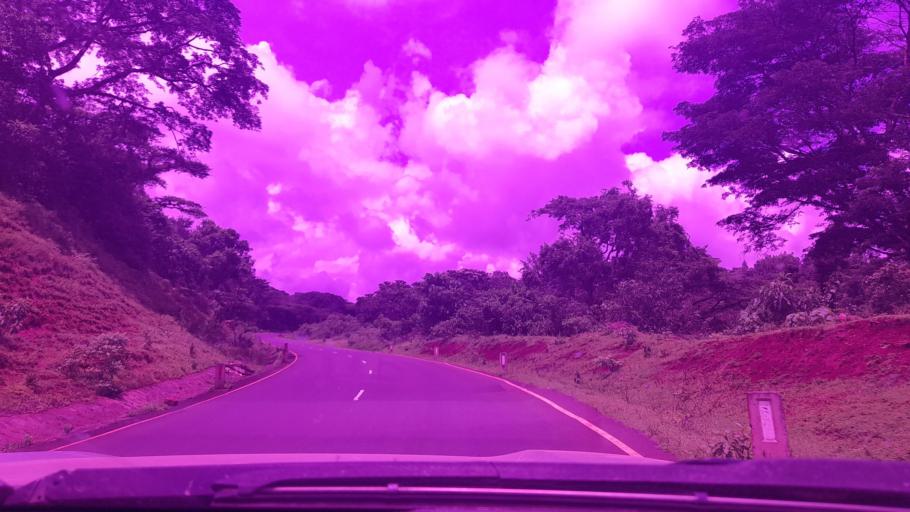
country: ET
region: Oromiya
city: Metu
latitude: 8.3372
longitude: 35.7397
